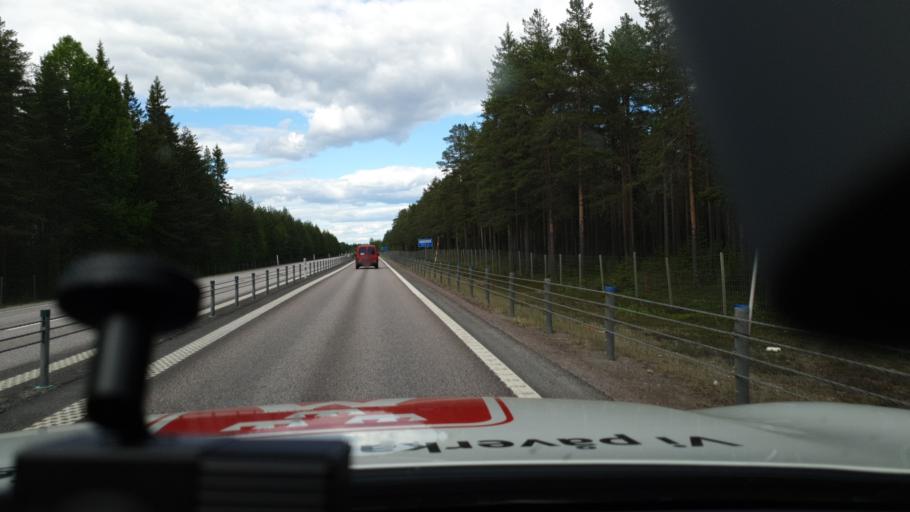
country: SE
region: Norrbotten
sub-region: Pitea Kommun
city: Rosvik
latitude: 65.5012
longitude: 21.7704
